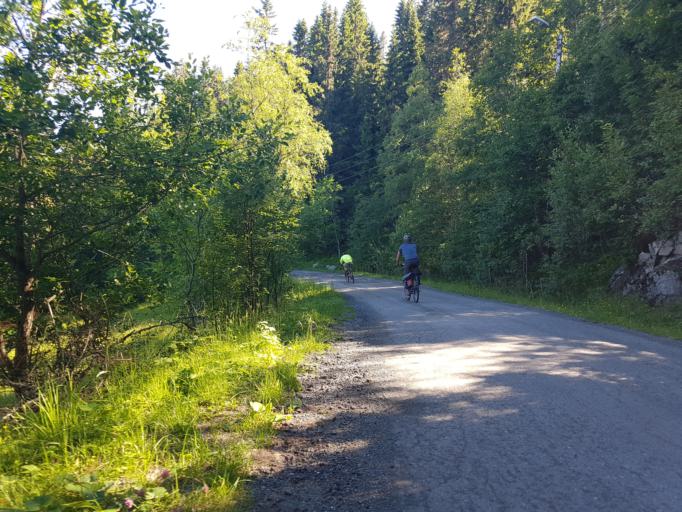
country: NO
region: Sor-Trondelag
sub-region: Trondheim
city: Trondheim
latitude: 63.4320
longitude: 10.2758
